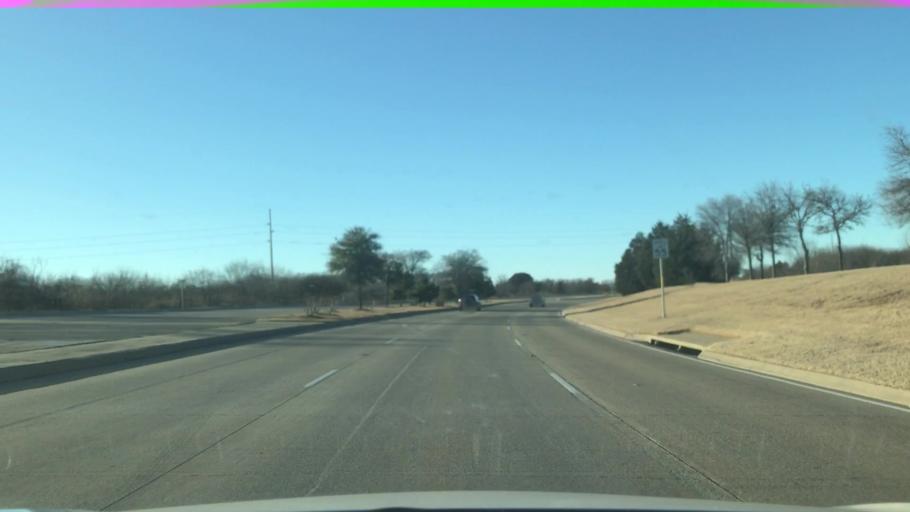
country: US
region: Texas
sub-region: Denton County
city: Flower Mound
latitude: 32.9877
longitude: -97.0599
